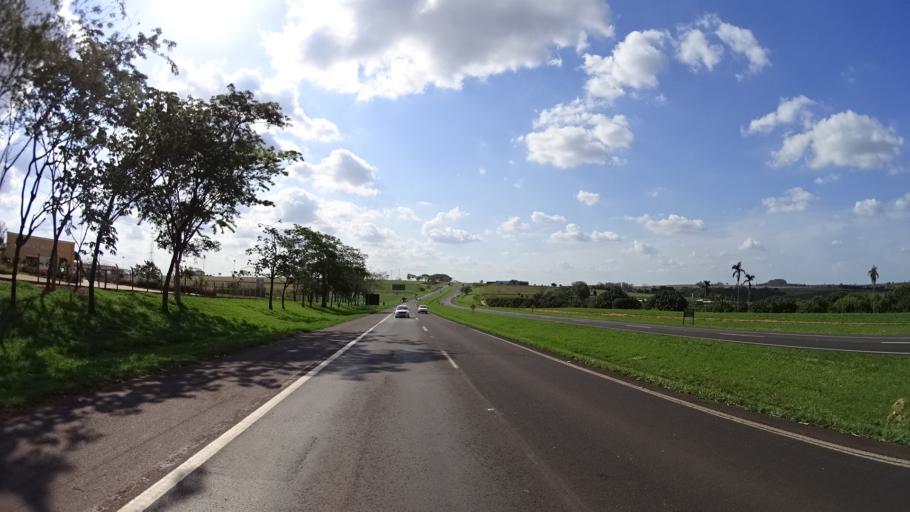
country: BR
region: Sao Paulo
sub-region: Guapiacu
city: Guapiacu
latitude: -20.9588
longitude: -49.2468
